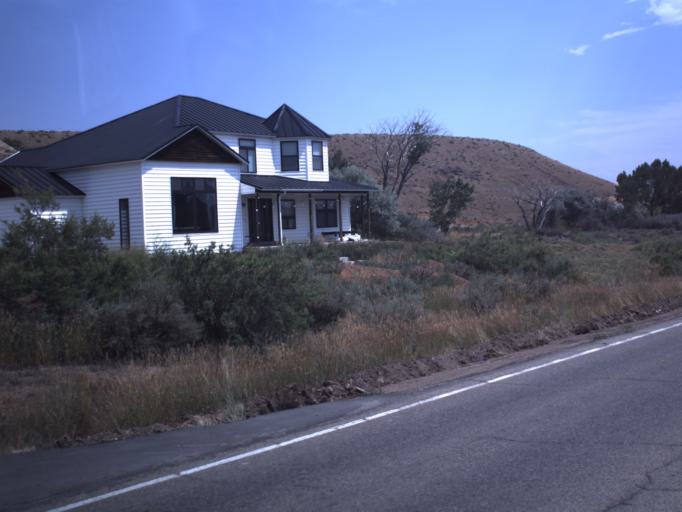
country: US
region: Utah
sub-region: Duchesne County
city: Roosevelt
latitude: 40.3227
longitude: -110.0164
